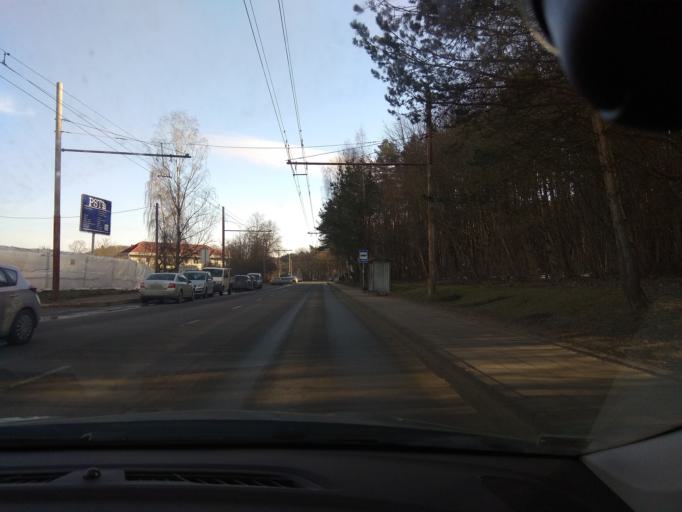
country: LT
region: Vilnius County
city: Lazdynai
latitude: 54.6452
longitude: 25.1948
